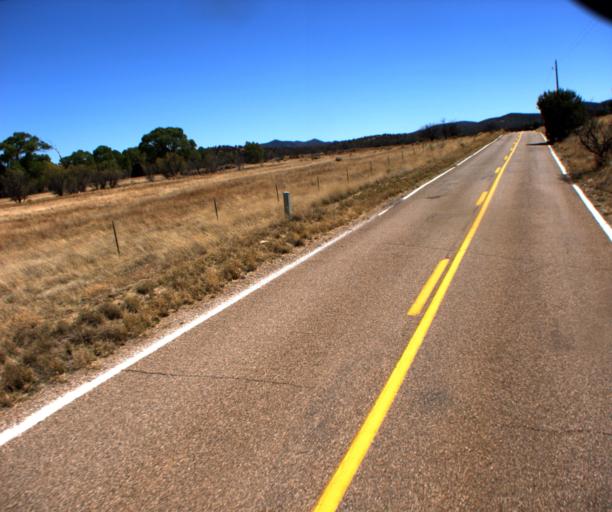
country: US
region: Arizona
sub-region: Cochise County
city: Huachuca City
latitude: 31.5503
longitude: -110.5292
